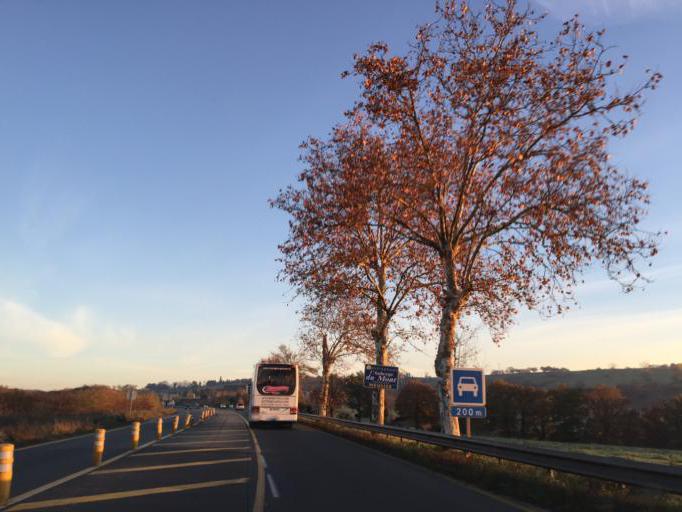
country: FR
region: Rhone-Alpes
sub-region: Departement de la Loire
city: Neulise
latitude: 45.8799
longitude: 4.1766
